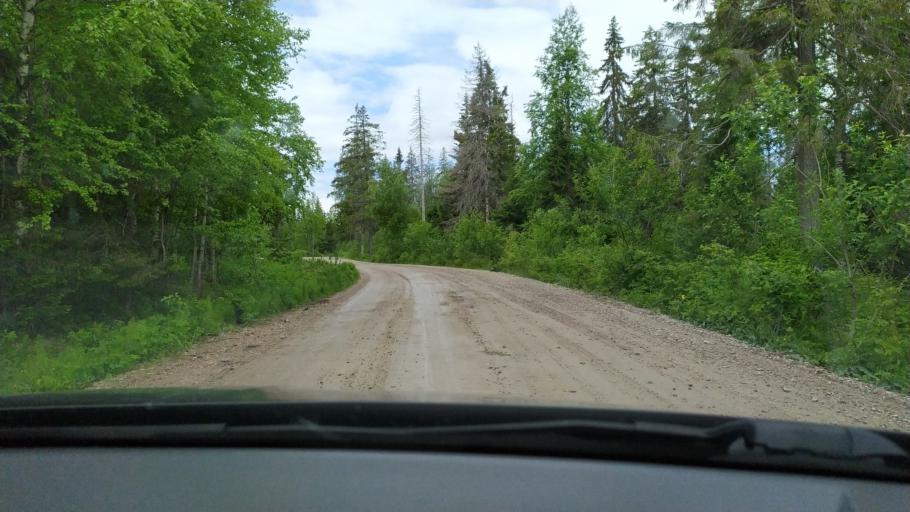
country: RU
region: Perm
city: Gremyachinsk
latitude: 58.5107
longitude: 57.8166
